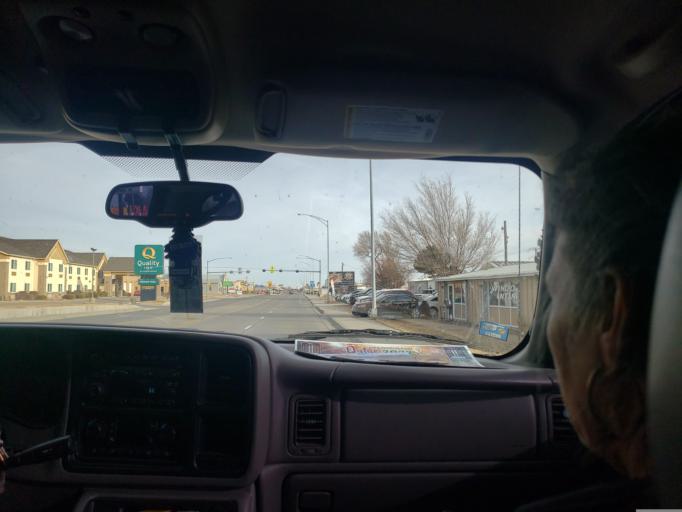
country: US
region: Kansas
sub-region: Ford County
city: Dodge City
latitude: 37.7541
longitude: -100.0422
